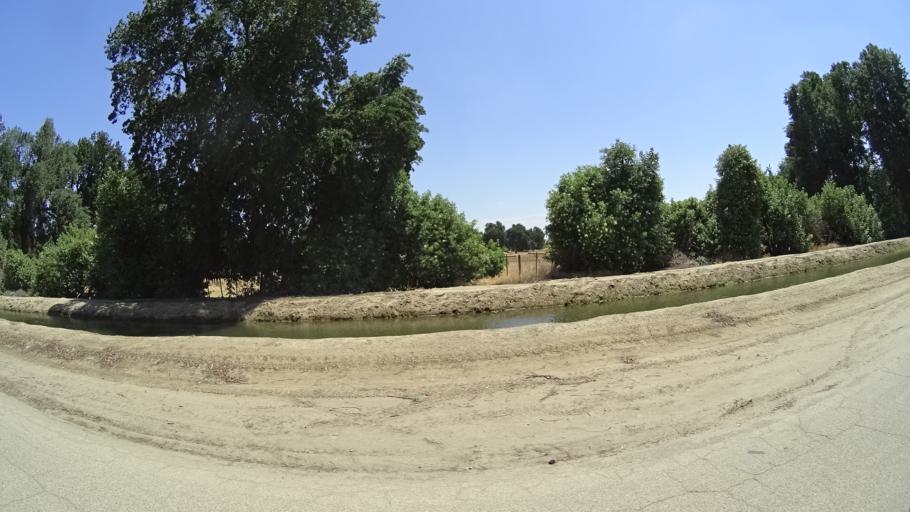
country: US
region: California
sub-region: Fresno County
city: Kingsburg
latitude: 36.4903
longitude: -119.5390
